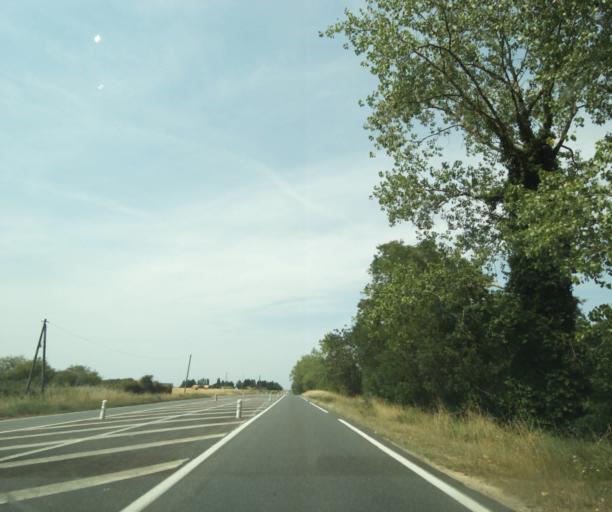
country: FR
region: Centre
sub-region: Departement d'Indre-et-Loire
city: Sainte-Maure-de-Touraine
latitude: 47.1461
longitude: 0.6470
